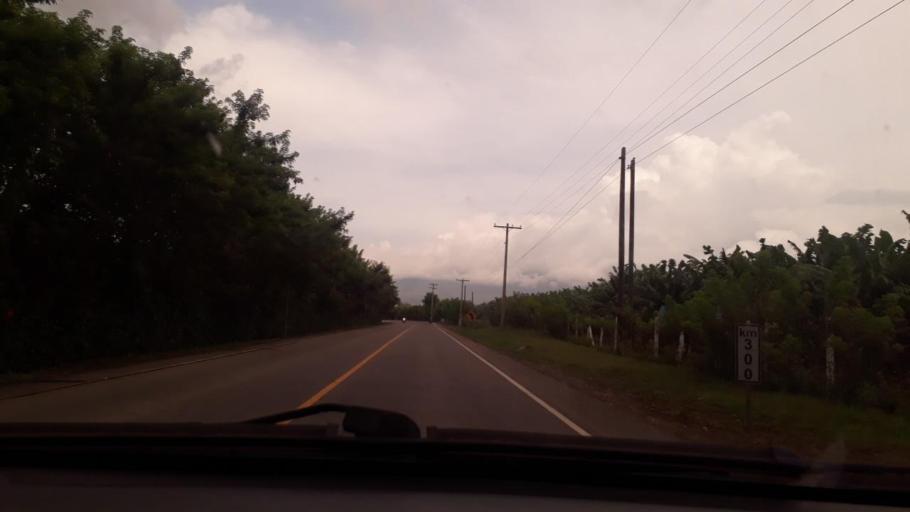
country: HN
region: Cortes
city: Potrerillos
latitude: 15.6375
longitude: -88.4142
